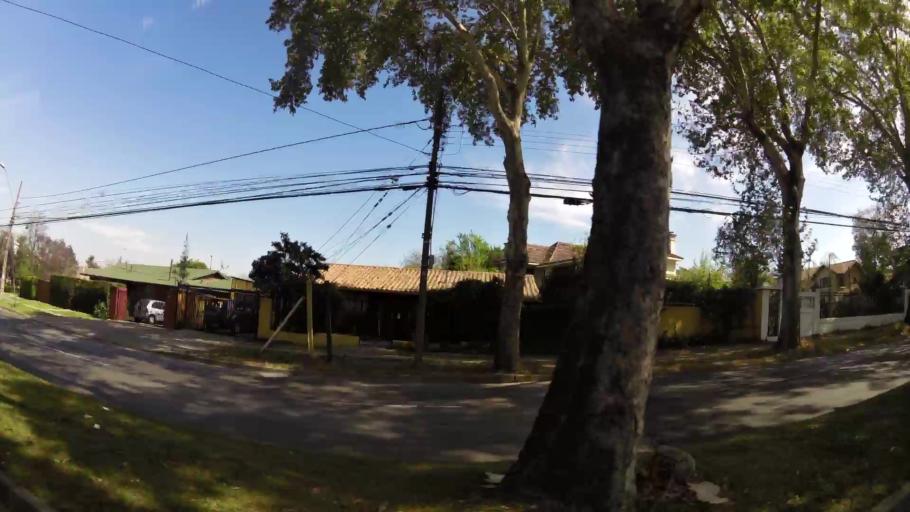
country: CL
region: Santiago Metropolitan
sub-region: Provincia de Santiago
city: Villa Presidente Frei, Nunoa, Santiago, Chile
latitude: -33.4441
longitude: -70.5360
